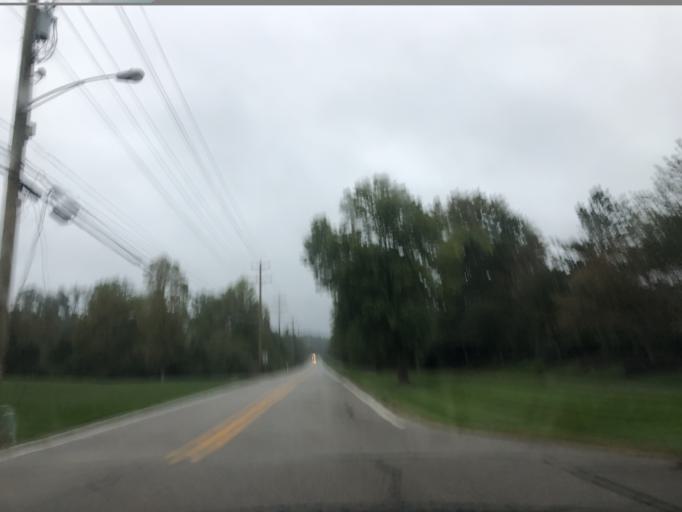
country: US
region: Ohio
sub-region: Hamilton County
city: The Village of Indian Hill
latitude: 39.2419
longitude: -84.3108
